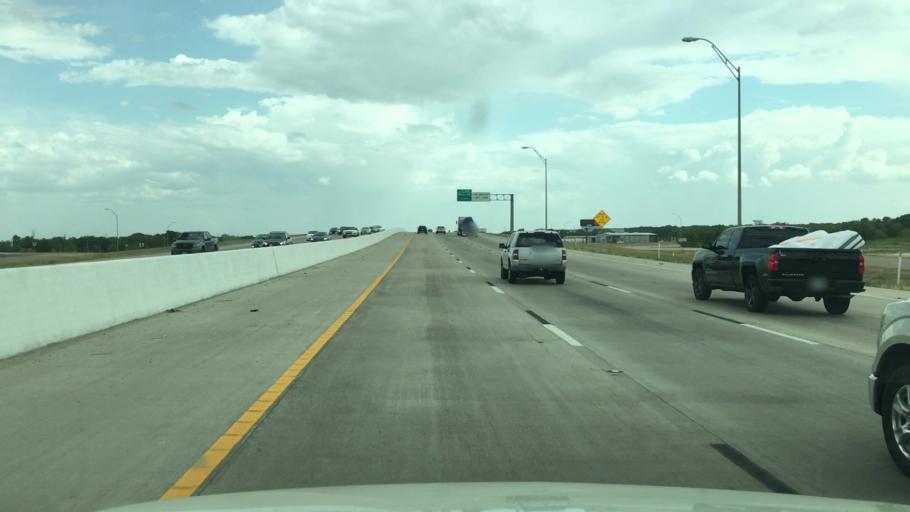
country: US
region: Texas
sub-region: McLennan County
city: West
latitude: 31.7314
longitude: -97.1032
